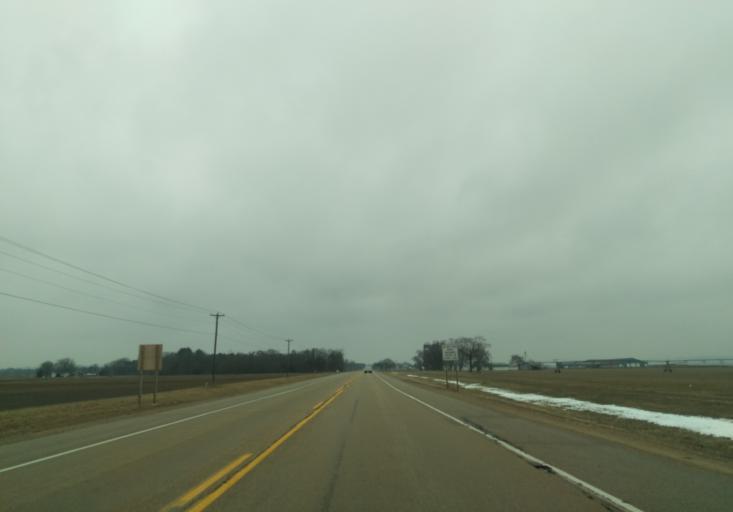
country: US
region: Wisconsin
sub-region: Sauk County
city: Spring Green
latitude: 43.1898
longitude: -90.1158
